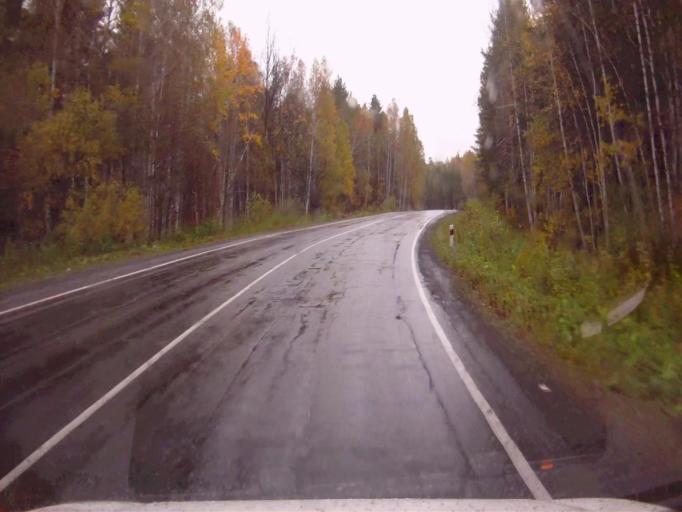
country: RU
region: Chelyabinsk
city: Verkhniy Ufaley
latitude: 55.9624
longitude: 60.3809
